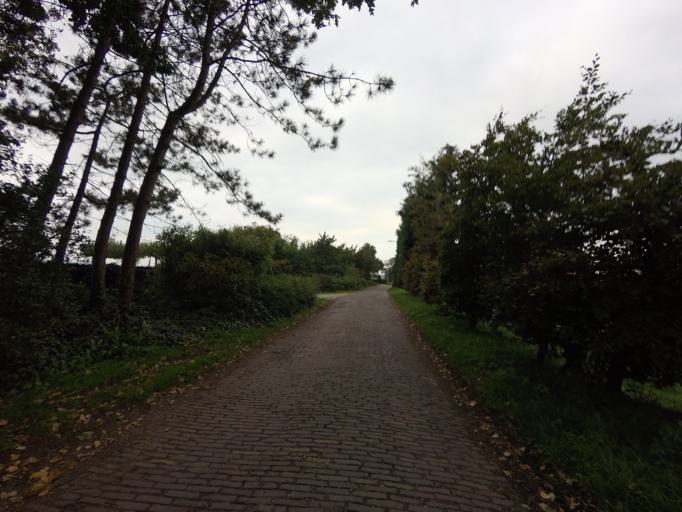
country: NL
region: South Holland
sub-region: Molenwaard
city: Liesveld
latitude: 51.8933
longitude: 4.7873
